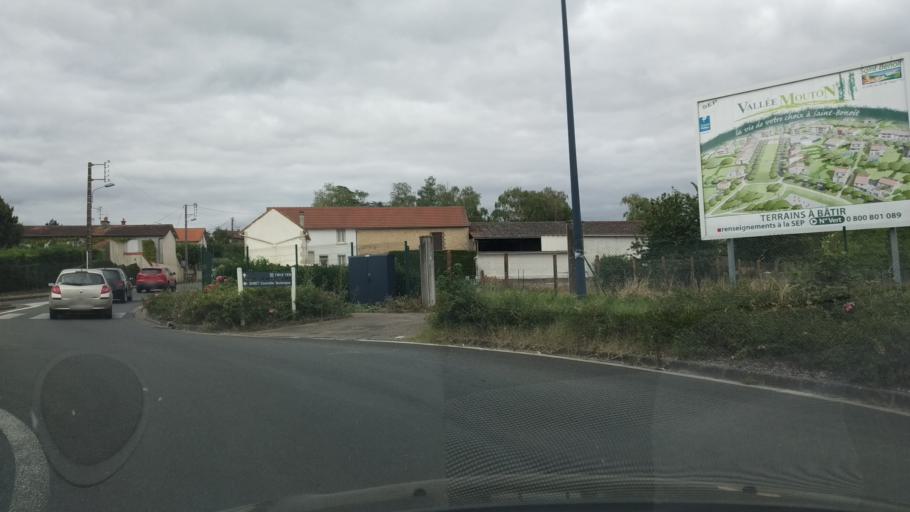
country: FR
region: Poitou-Charentes
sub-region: Departement de la Vienne
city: Saint-Benoit
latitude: 46.5590
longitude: 0.3555
